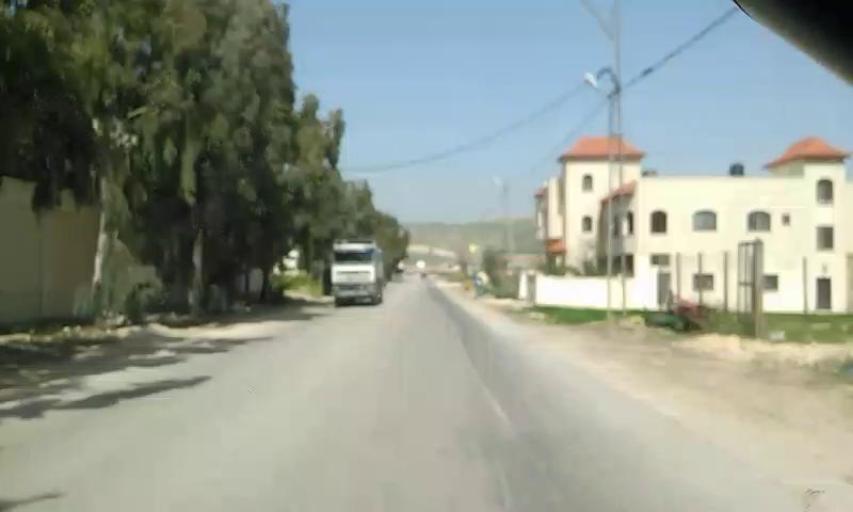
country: PS
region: West Bank
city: Az Zababidah
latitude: 32.3922
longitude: 35.3210
